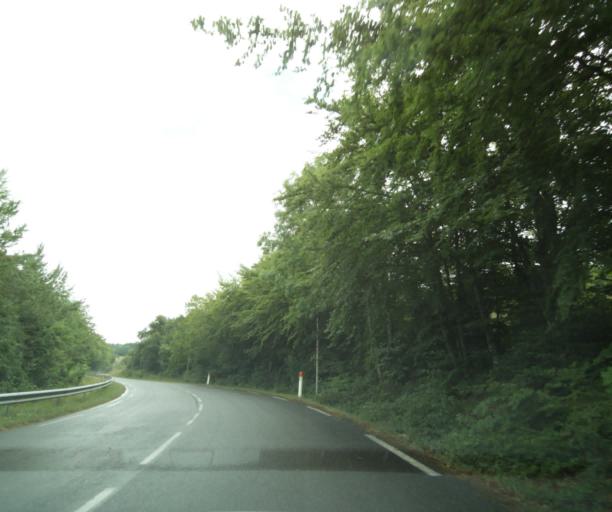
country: FR
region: Languedoc-Roussillon
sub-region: Departement de la Lozere
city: La Canourgue
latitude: 44.4067
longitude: 3.1464
